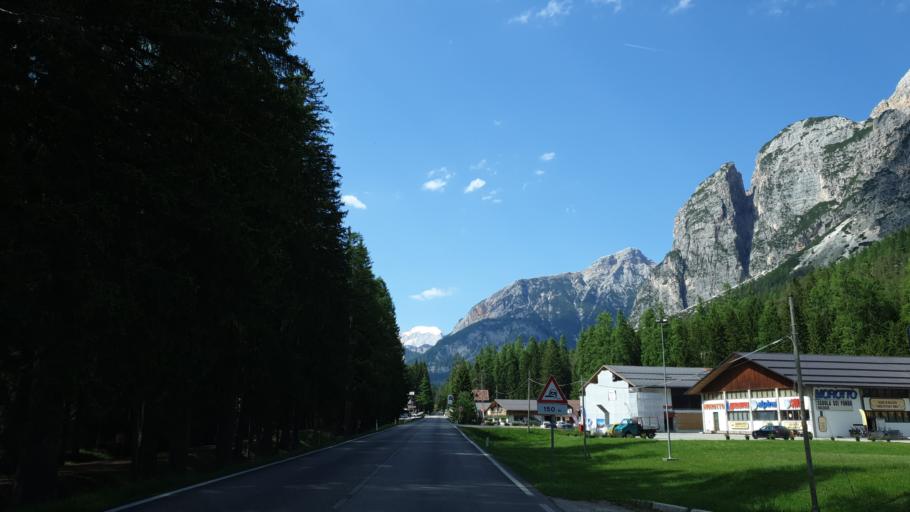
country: IT
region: Veneto
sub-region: Provincia di Belluno
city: Cortina d'Ampezzo
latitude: 46.5733
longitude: 12.1173
